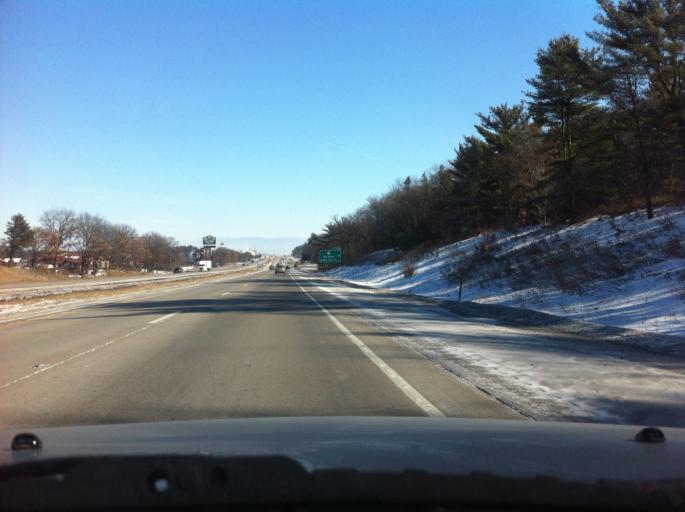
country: US
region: Wisconsin
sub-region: Sauk County
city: Lake Delton
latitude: 43.5889
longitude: -89.8091
